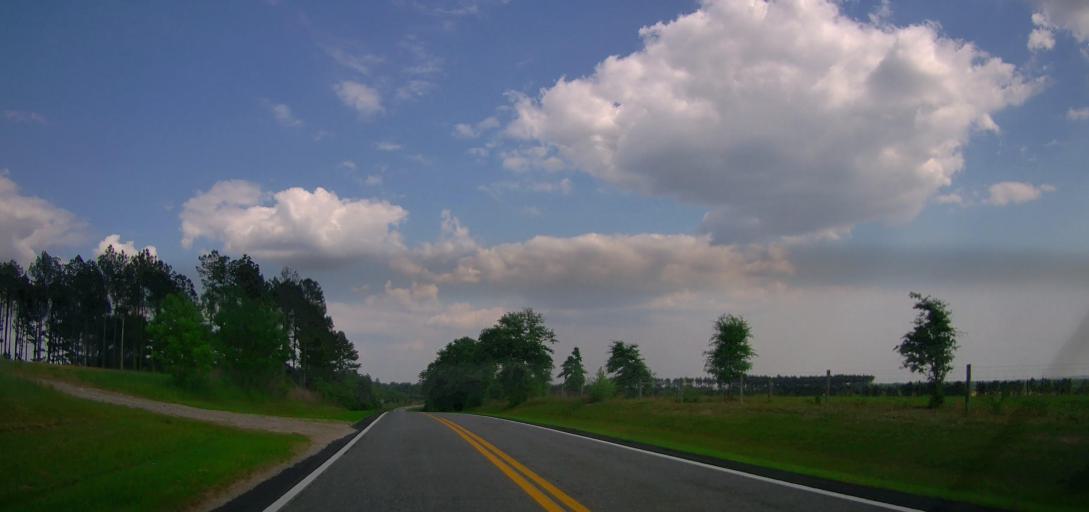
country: US
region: Georgia
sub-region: Laurens County
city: East Dublin
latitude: 32.6258
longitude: -82.8847
